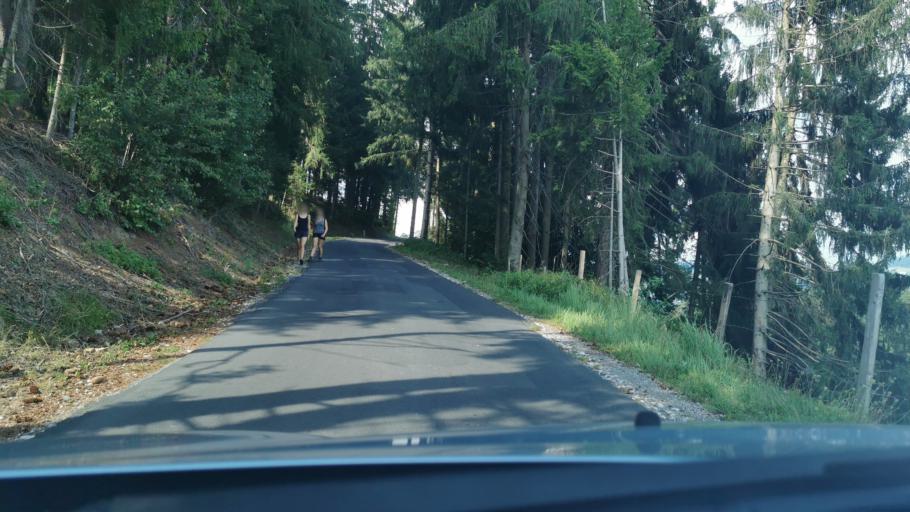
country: AT
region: Styria
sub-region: Politischer Bezirk Weiz
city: Strallegg
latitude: 47.4045
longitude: 15.6904
